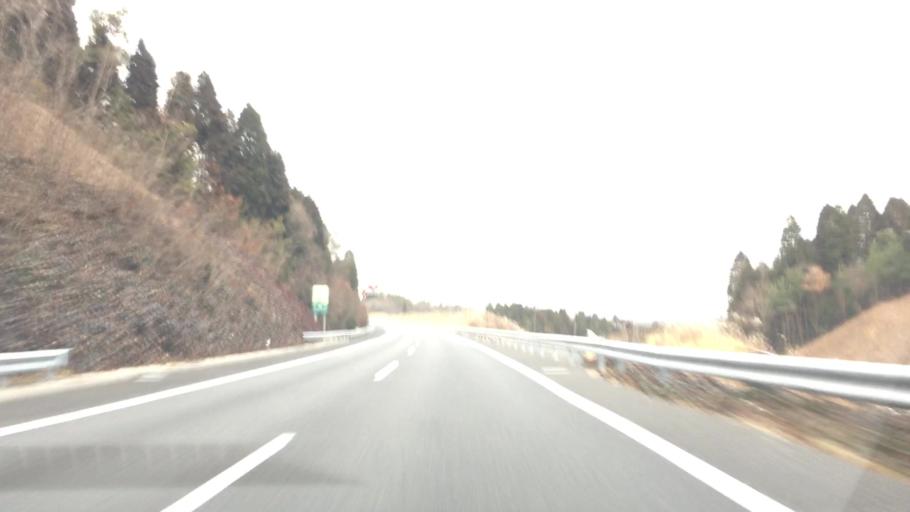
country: JP
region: Gifu
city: Tajimi
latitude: 35.2970
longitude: 137.1801
